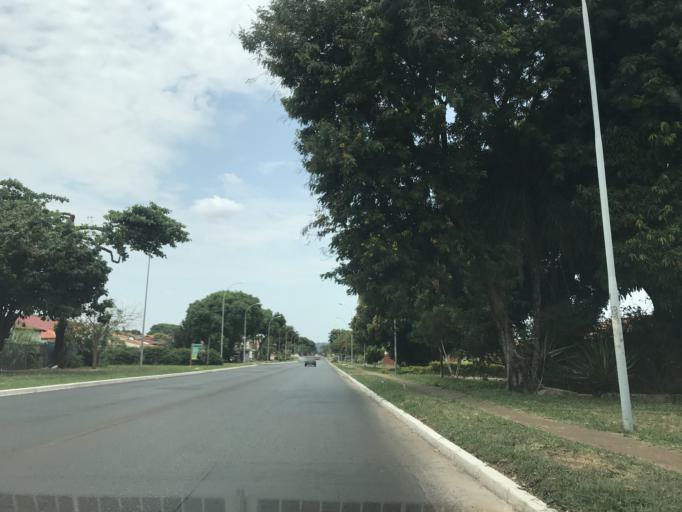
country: BR
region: Federal District
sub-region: Brasilia
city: Brasilia
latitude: -15.6483
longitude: -47.8034
